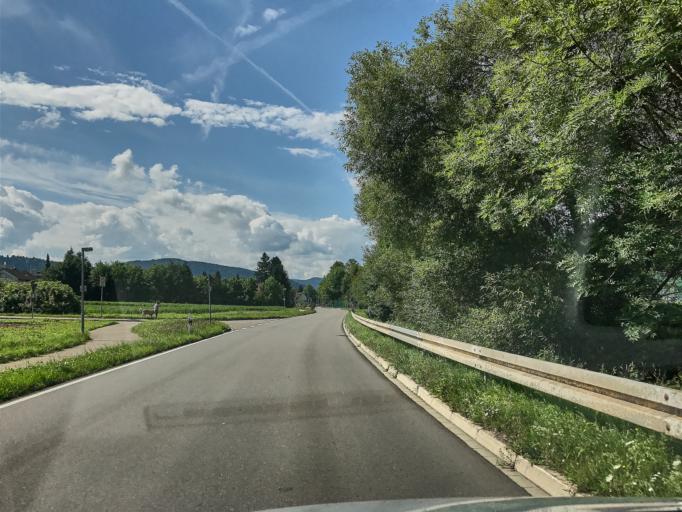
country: DE
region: Baden-Wuerttemberg
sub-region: Freiburg Region
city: Biberach
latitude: 48.3535
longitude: 8.0616
